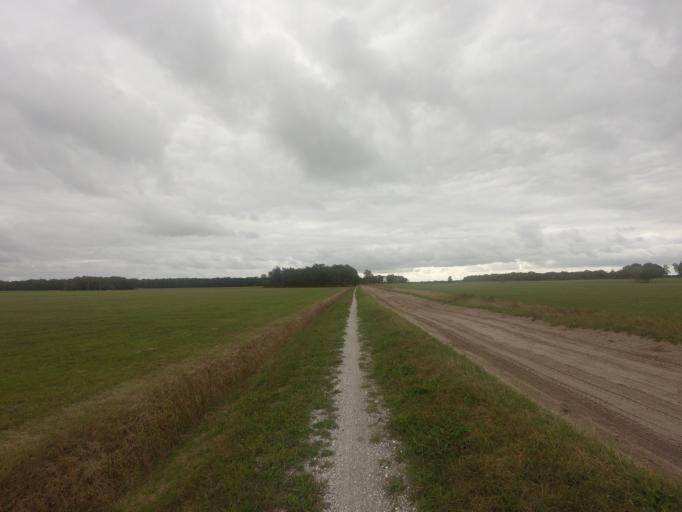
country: NL
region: Friesland
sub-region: Gemeente Weststellingwerf
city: Noordwolde
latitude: 52.9298
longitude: 6.1886
